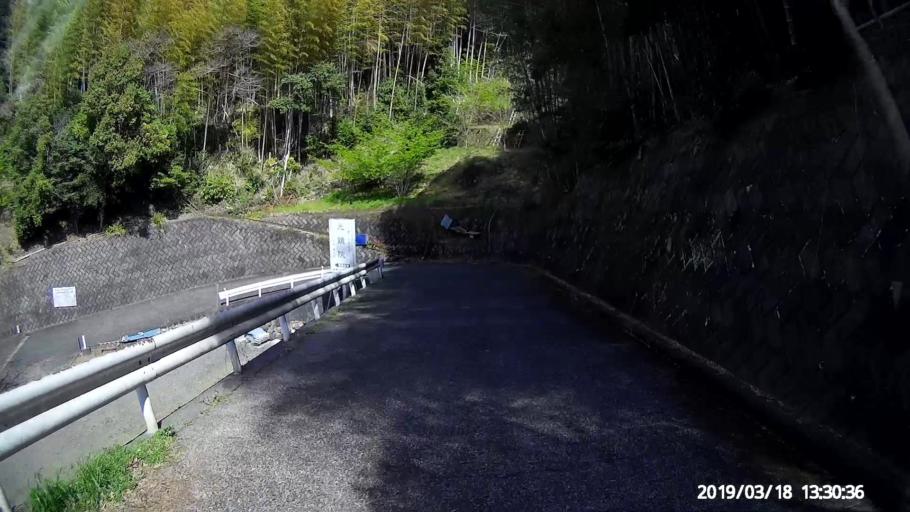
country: JP
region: Shizuoka
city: Shizuoka-shi
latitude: 35.0166
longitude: 138.4263
